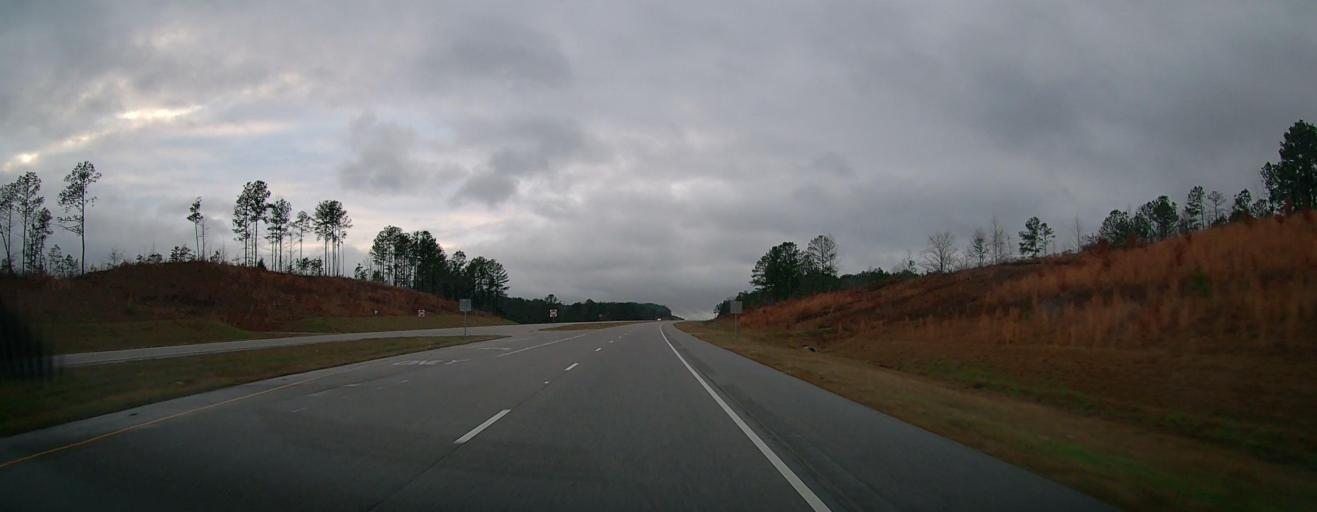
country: US
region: Alabama
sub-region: Bibb County
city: Centreville
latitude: 32.9470
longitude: -87.0959
